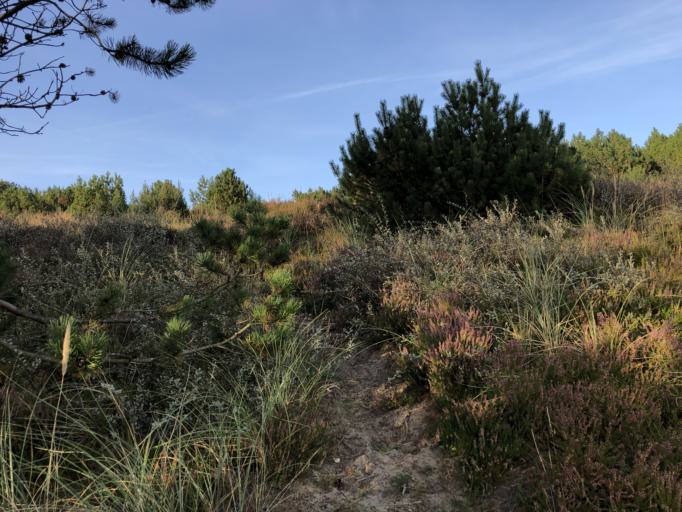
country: DK
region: Central Jutland
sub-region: Holstebro Kommune
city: Ulfborg
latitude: 56.2467
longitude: 8.4517
